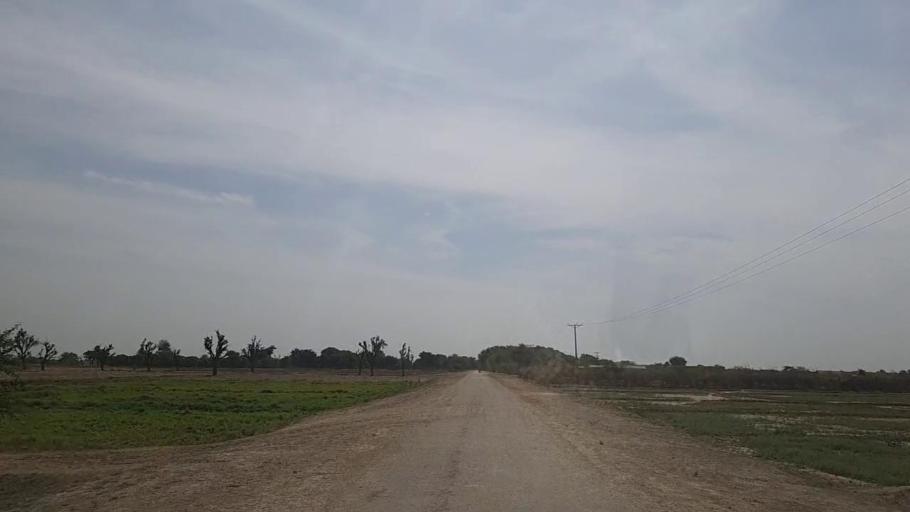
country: PK
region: Sindh
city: Samaro
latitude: 25.2348
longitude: 69.4733
